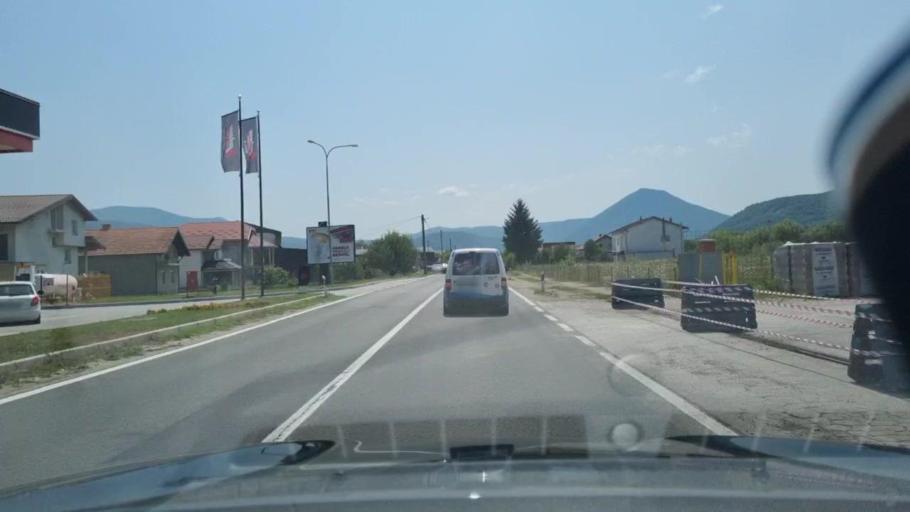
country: BA
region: Federation of Bosnia and Herzegovina
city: Bihac
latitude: 44.7898
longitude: 15.9295
